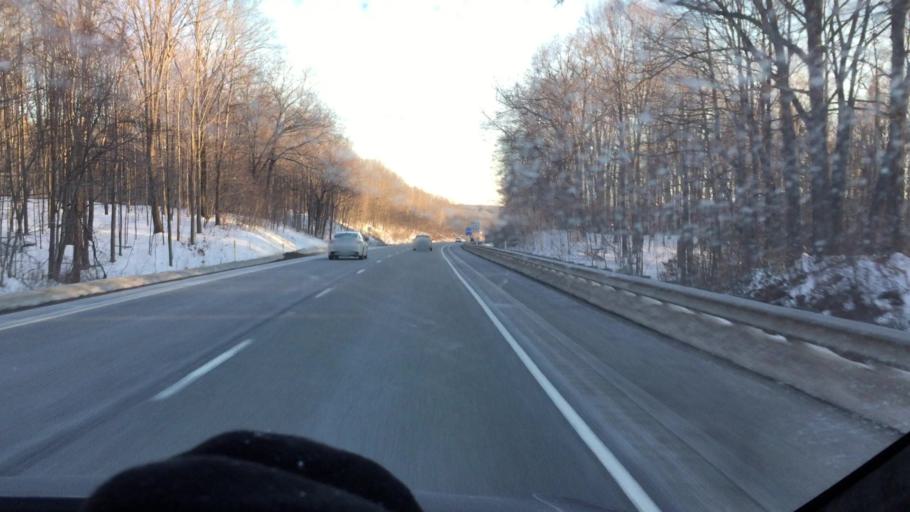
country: US
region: Pennsylvania
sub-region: Crawford County
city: Meadville
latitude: 41.7066
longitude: -80.1994
